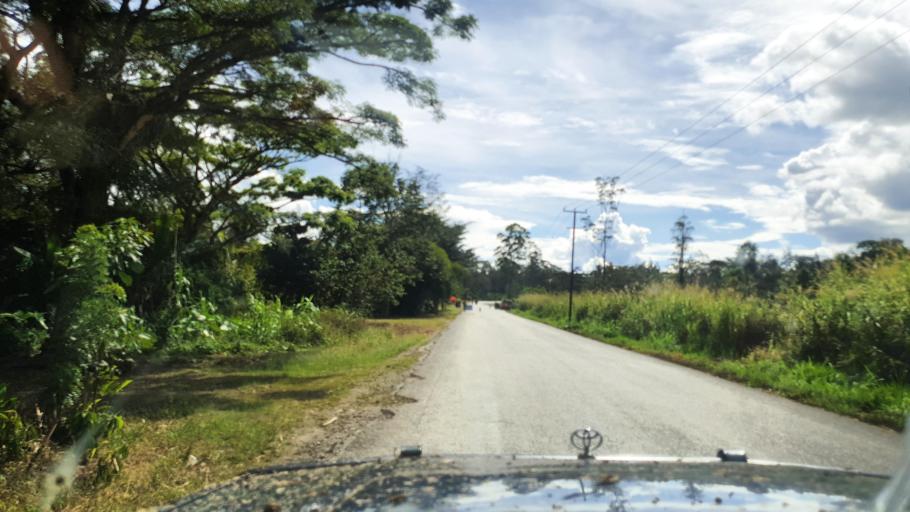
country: PG
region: Jiwaka
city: Minj
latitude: -5.8850
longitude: 144.7280
